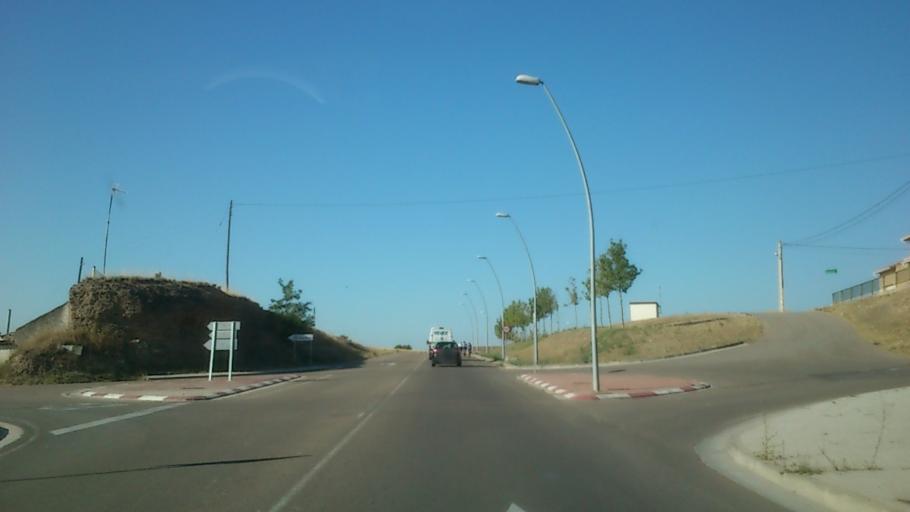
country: ES
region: Aragon
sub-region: Provincia de Zaragoza
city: Villanueva de Gallego
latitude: 41.7652
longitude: -0.8264
